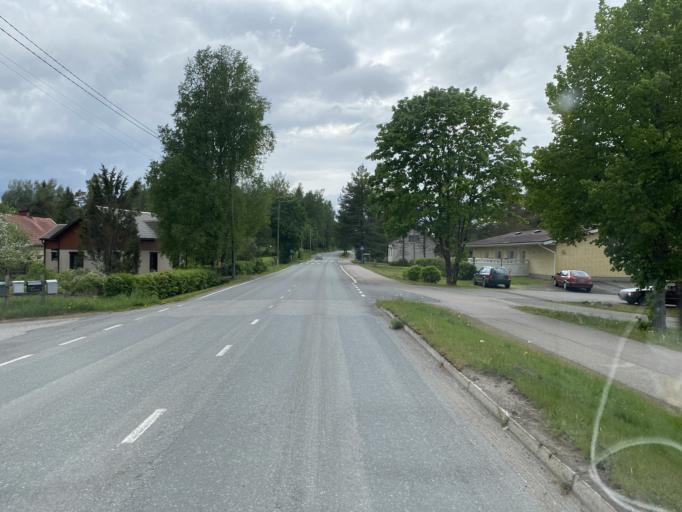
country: FI
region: Pirkanmaa
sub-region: Etelae-Pirkanmaa
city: Urjala
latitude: 61.0802
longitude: 23.5585
